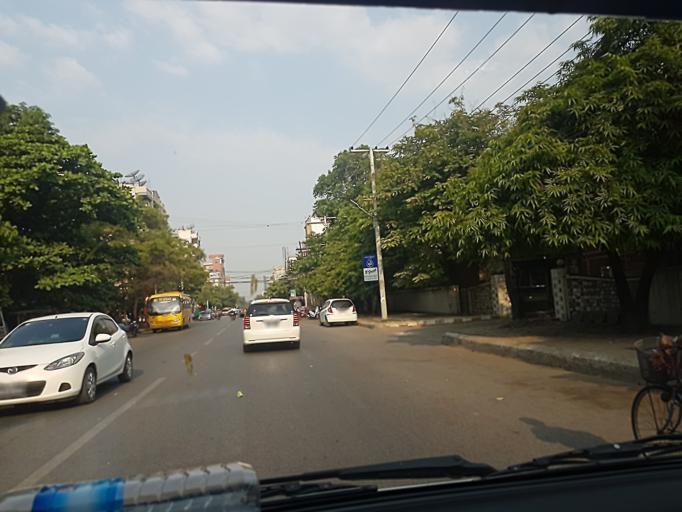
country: MM
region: Mandalay
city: Mandalay
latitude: 21.9886
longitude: 96.0839
